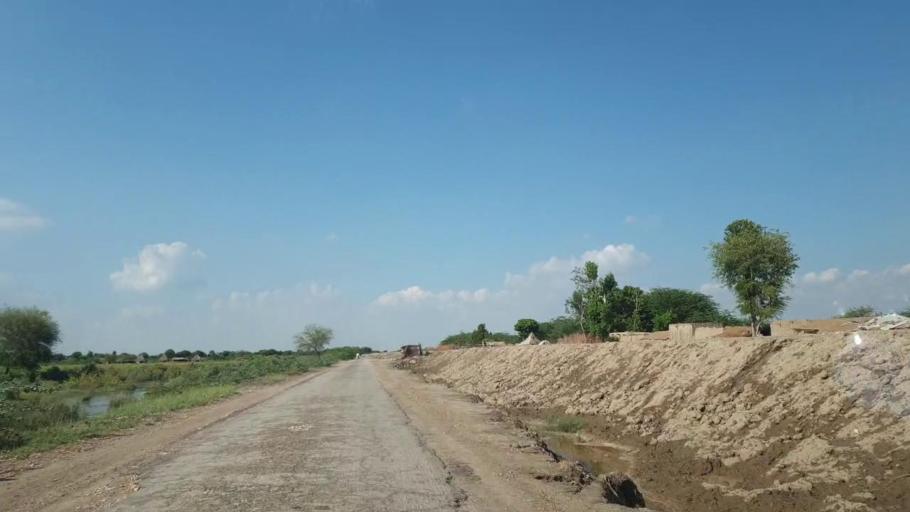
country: PK
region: Sindh
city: Pithoro
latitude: 25.6276
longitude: 69.4328
